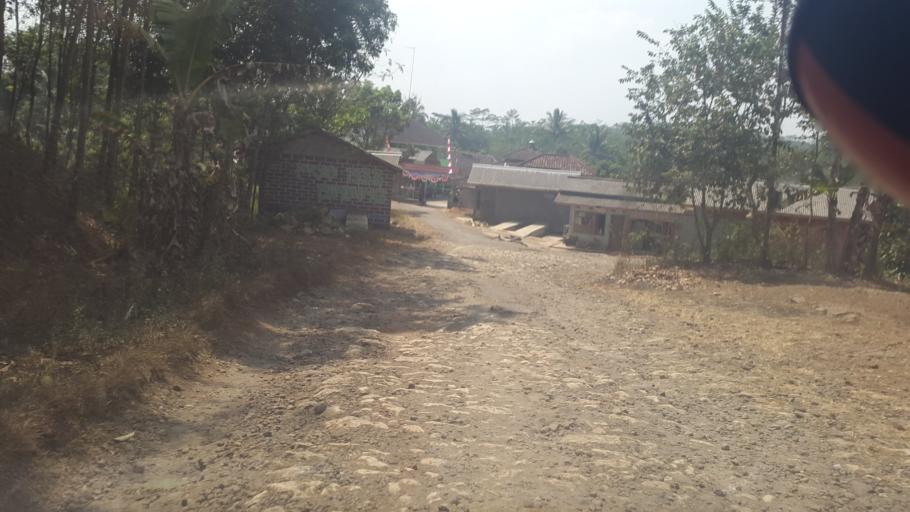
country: ID
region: West Java
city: Ciroyom
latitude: -7.0951
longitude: 106.8264
